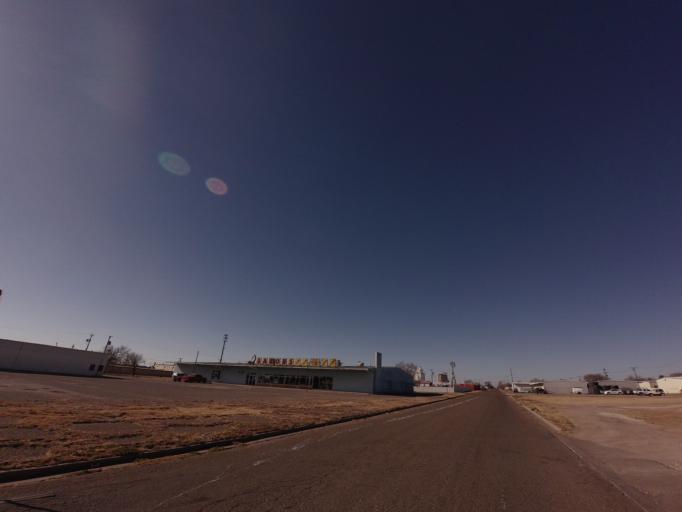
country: US
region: New Mexico
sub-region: Curry County
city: Clovis
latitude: 34.3997
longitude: -103.1878
